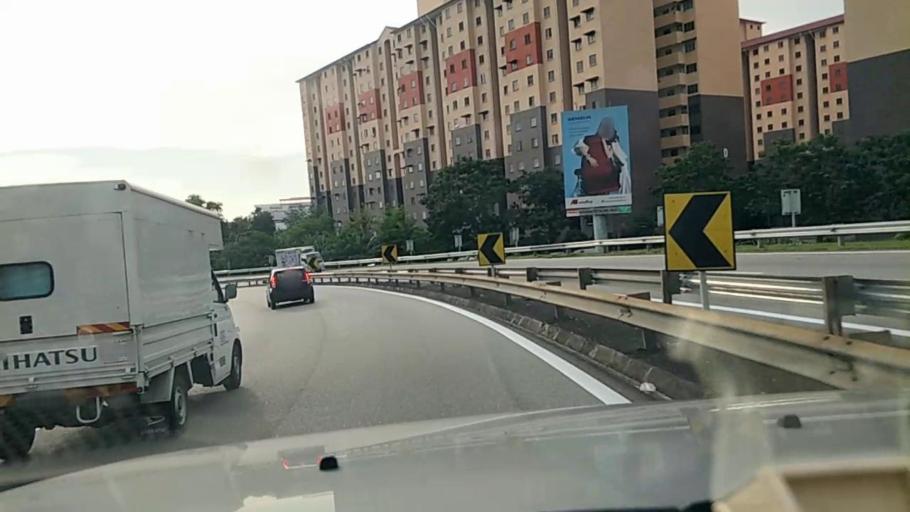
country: MY
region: Selangor
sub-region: Petaling
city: Petaling Jaya
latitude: 3.1070
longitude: 101.5896
